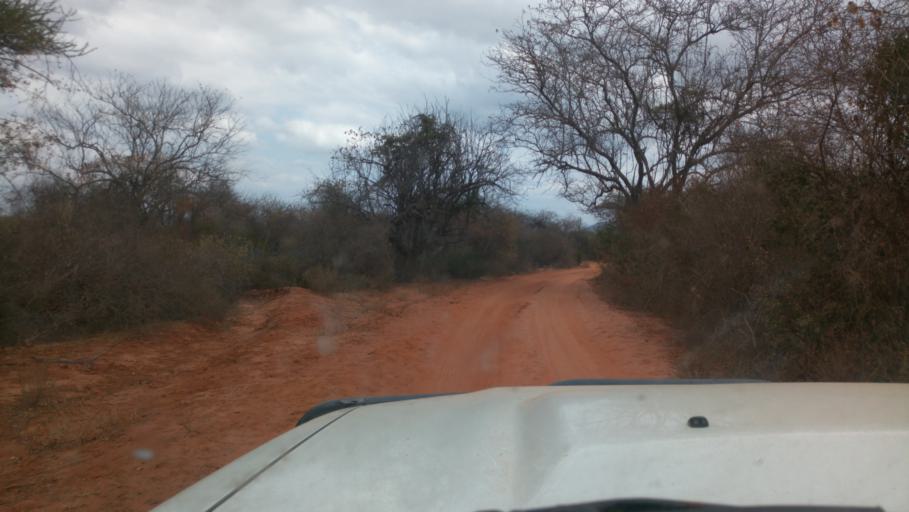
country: KE
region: Kitui
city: Kitui
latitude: -1.9081
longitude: 38.4196
